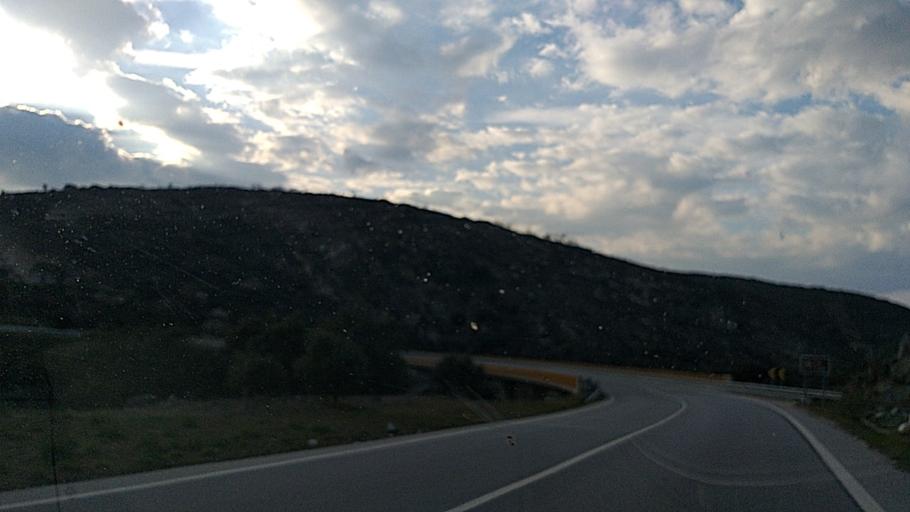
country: ES
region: Castille and Leon
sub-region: Provincia de Salamanca
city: Aldea del Obispo
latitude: 40.7029
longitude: -6.9300
